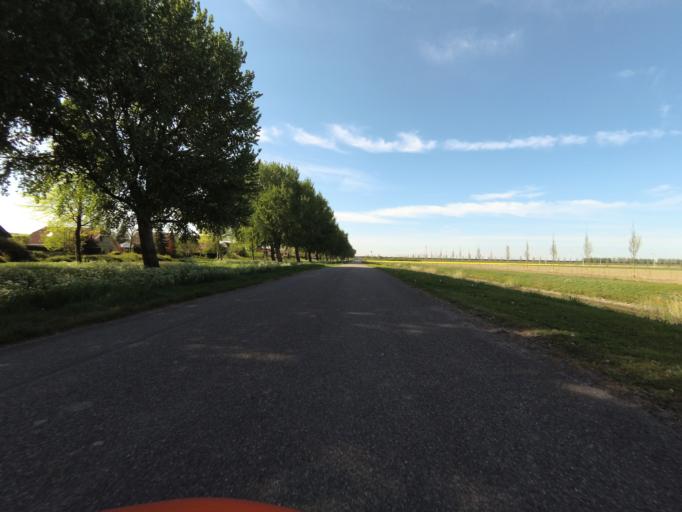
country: NL
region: Flevoland
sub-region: Gemeente Dronten
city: Dronten
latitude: 52.5440
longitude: 5.7019
